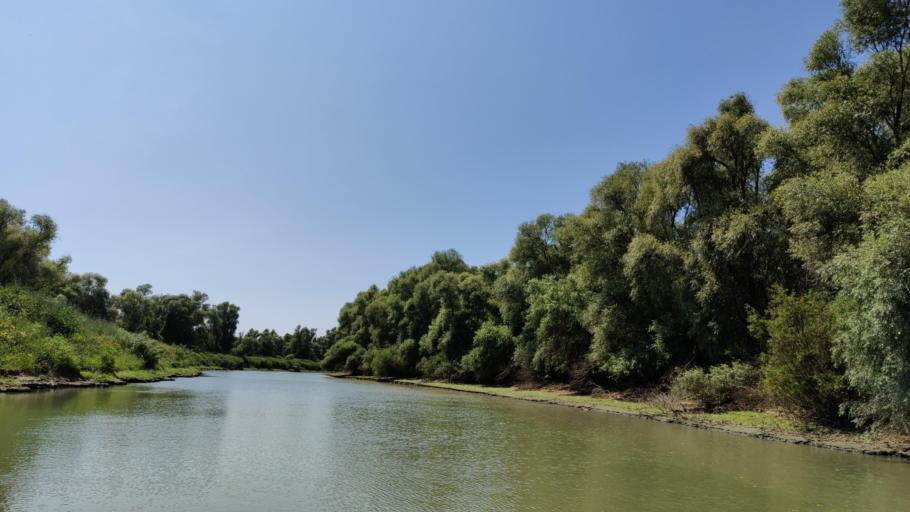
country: RO
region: Tulcea
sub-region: Comuna Pardina
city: Pardina
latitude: 45.2558
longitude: 28.9565
